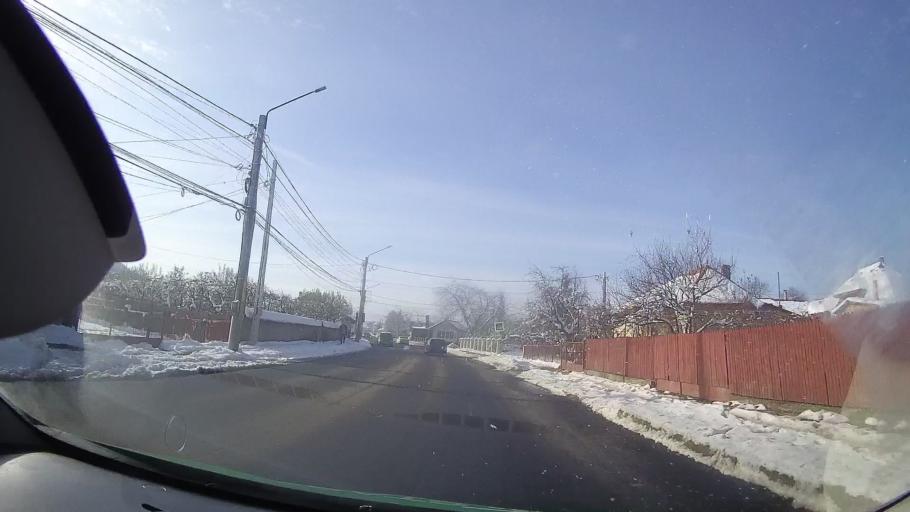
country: RO
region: Neamt
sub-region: Oras Targu Neamt
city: Targu Neamt
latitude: 47.2083
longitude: 26.3816
